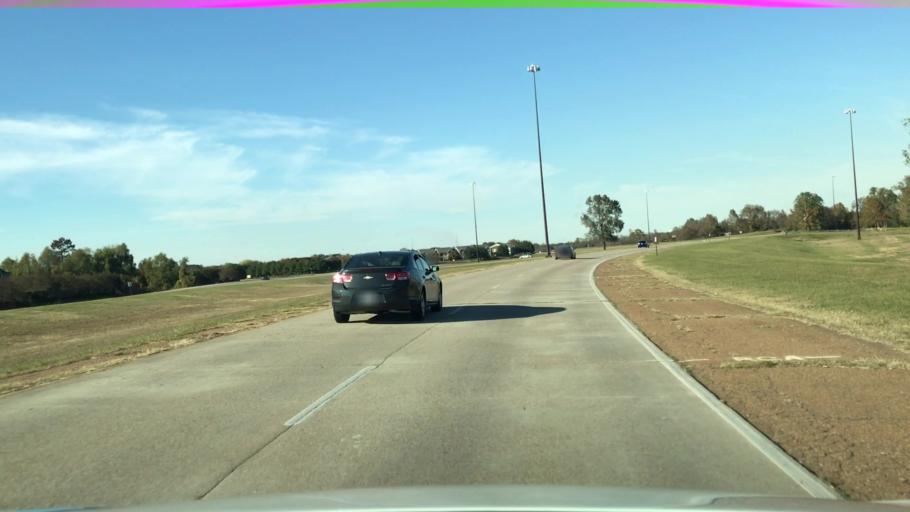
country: US
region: Louisiana
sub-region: Bossier Parish
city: Bossier City
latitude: 32.4659
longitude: -93.6851
